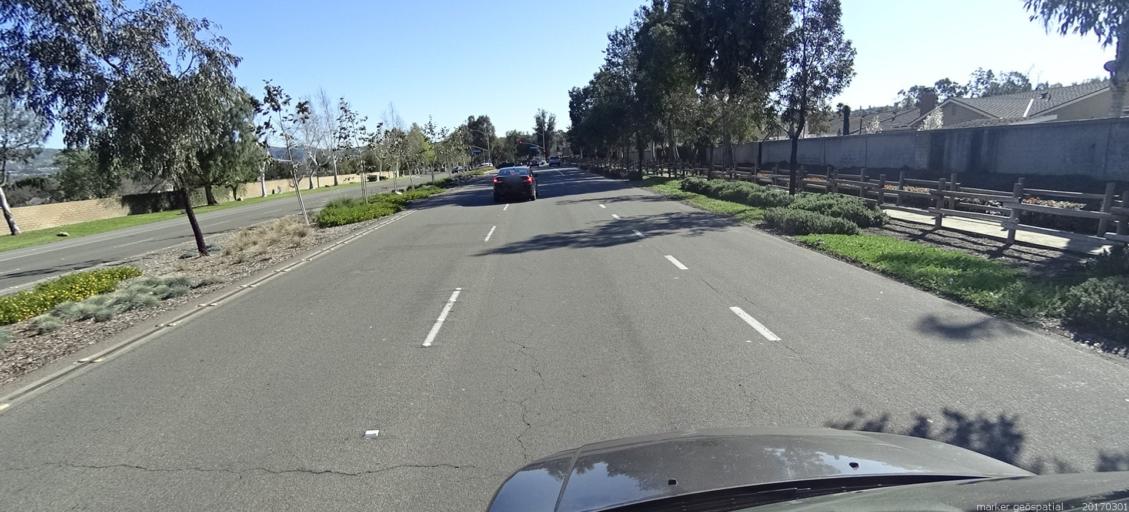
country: US
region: California
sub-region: Orange County
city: Yorba Linda
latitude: 33.8533
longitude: -117.7806
